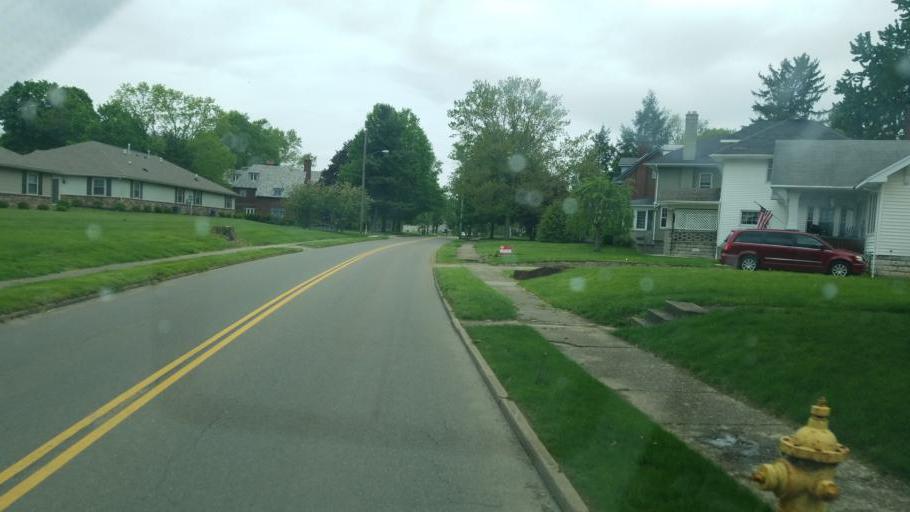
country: US
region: Ohio
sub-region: Coshocton County
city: Coshocton
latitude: 40.2635
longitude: -81.8468
